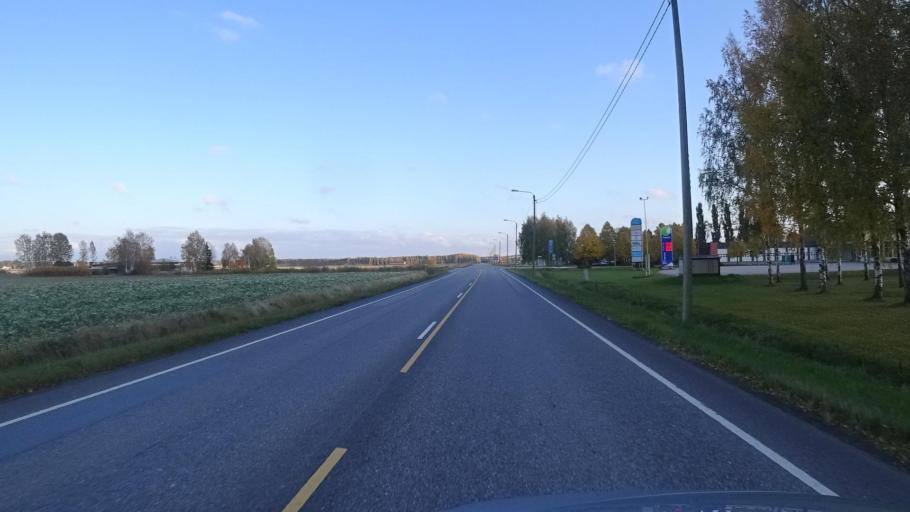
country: FI
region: Satakunta
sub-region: Rauma
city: Saekylae
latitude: 61.0495
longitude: 22.3487
